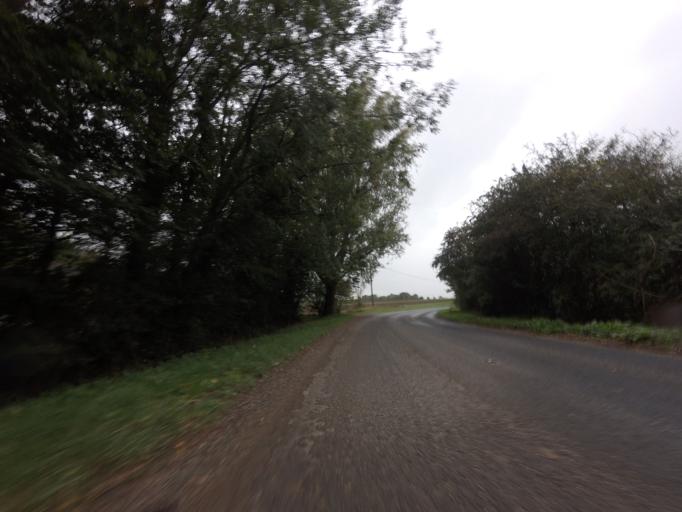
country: GB
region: England
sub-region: Cambridgeshire
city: Wimpole
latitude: 52.1839
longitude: -0.0536
